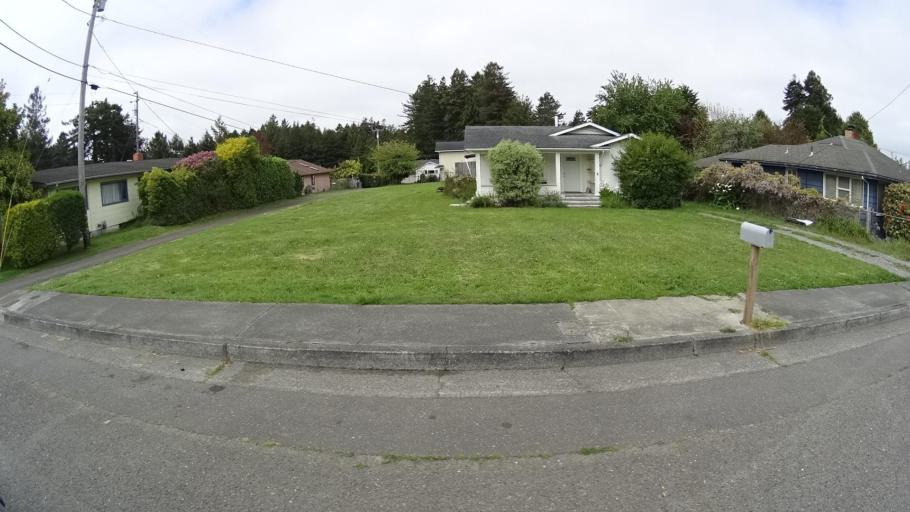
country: US
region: California
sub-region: Humboldt County
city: Cutten
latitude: 40.7645
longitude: -124.1494
